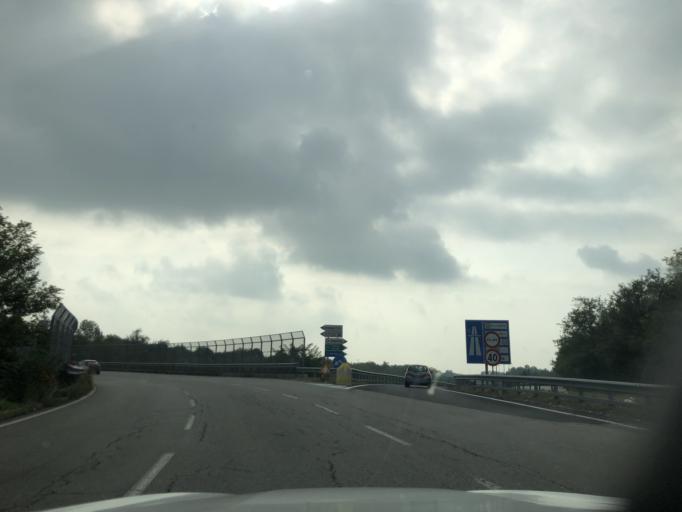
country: IT
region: Lombardy
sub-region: Provincia di Varese
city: Vizzola Ticino
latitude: 45.6255
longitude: 8.7053
